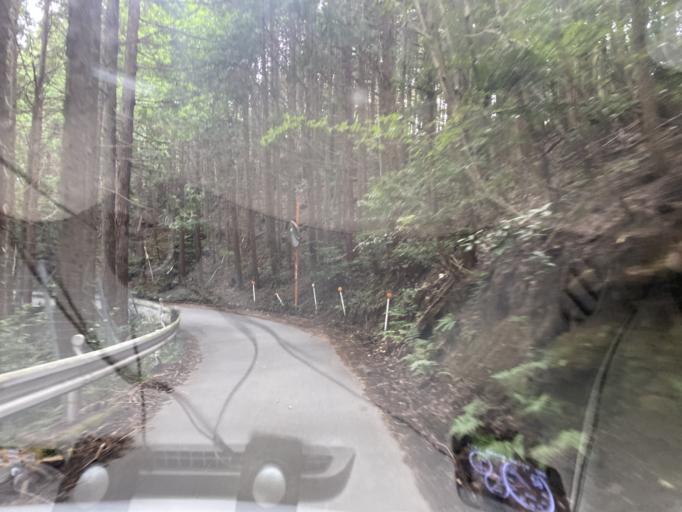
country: JP
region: Nara
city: Nara-shi
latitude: 34.6808
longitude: 135.8951
